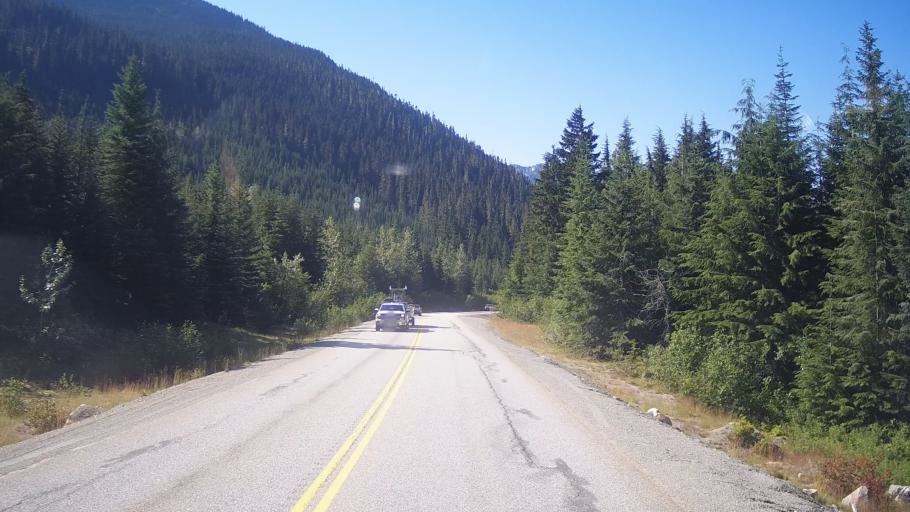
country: CA
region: British Columbia
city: Pemberton
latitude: 50.3640
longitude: -122.5216
